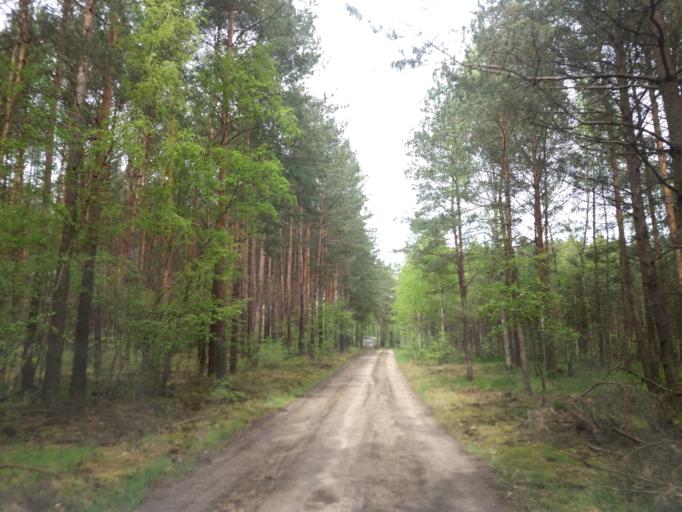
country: PL
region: Lubusz
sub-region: Powiat strzelecko-drezdenecki
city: Dobiegniew
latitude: 52.9903
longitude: 15.7300
